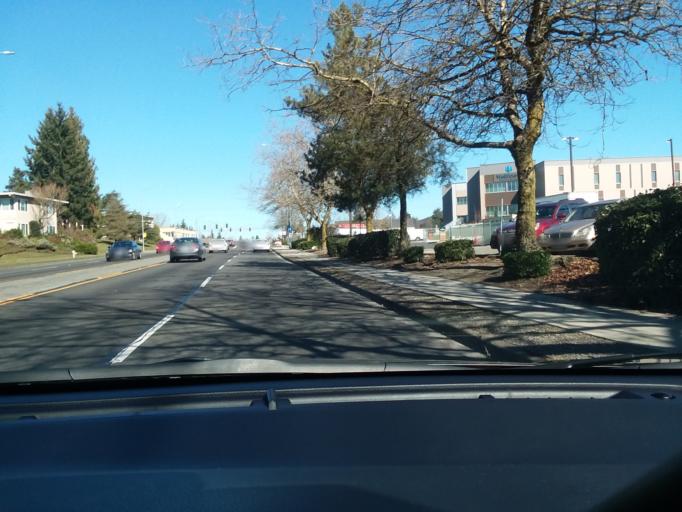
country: US
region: Washington
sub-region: Pierce County
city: Fircrest
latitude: 47.2412
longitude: -122.4822
